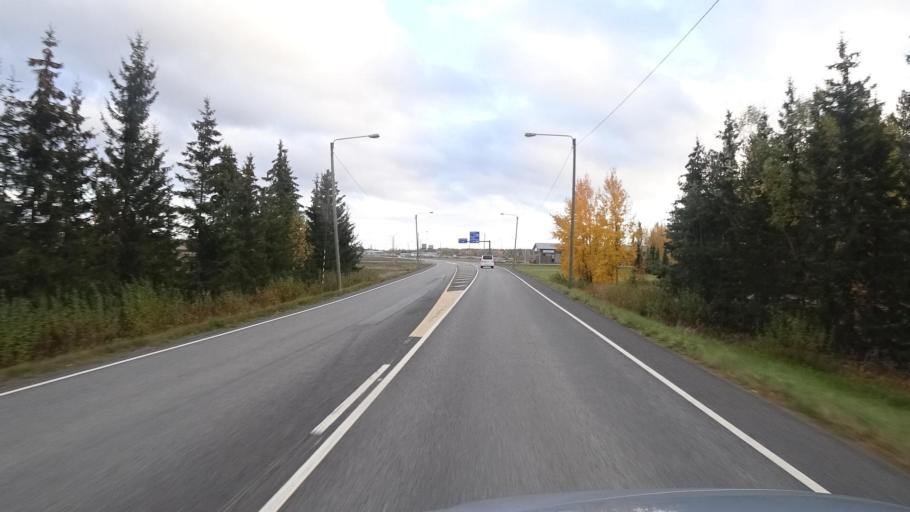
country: FI
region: Varsinais-Suomi
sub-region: Loimaa
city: Loimaa
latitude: 60.8712
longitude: 23.0013
